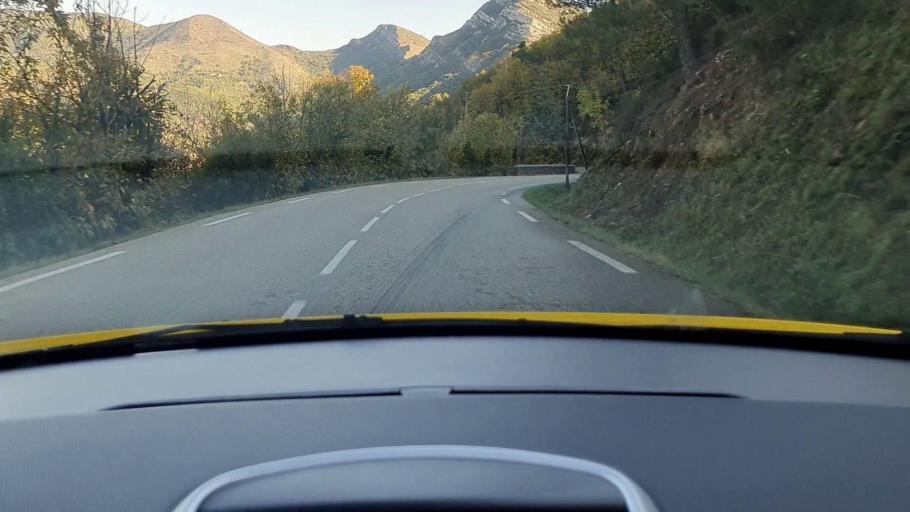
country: FR
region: Languedoc-Roussillon
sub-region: Departement du Gard
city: Sumene
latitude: 43.9860
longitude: 3.7034
